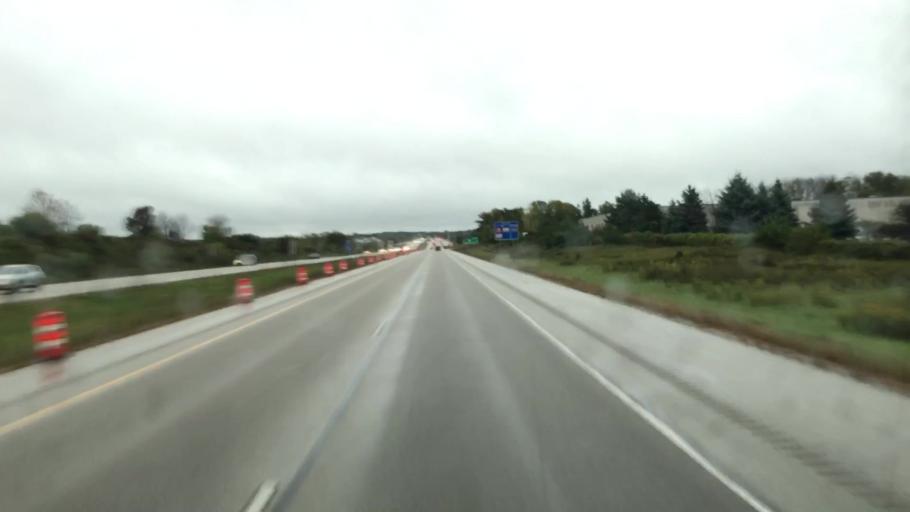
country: US
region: Wisconsin
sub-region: Waukesha County
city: New Berlin
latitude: 42.9457
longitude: -88.1195
